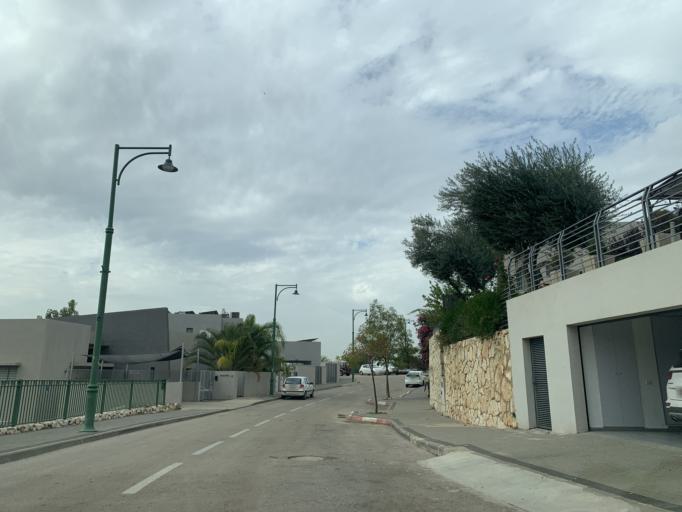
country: IL
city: Nirit
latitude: 32.1488
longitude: 34.9855
